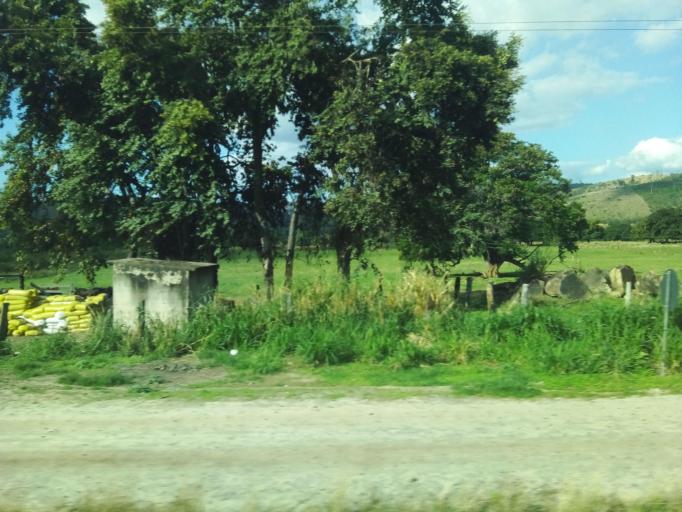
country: BR
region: Minas Gerais
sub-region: Conselheiro Pena
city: Conselheiro Pena
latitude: -19.1193
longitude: -41.5028
